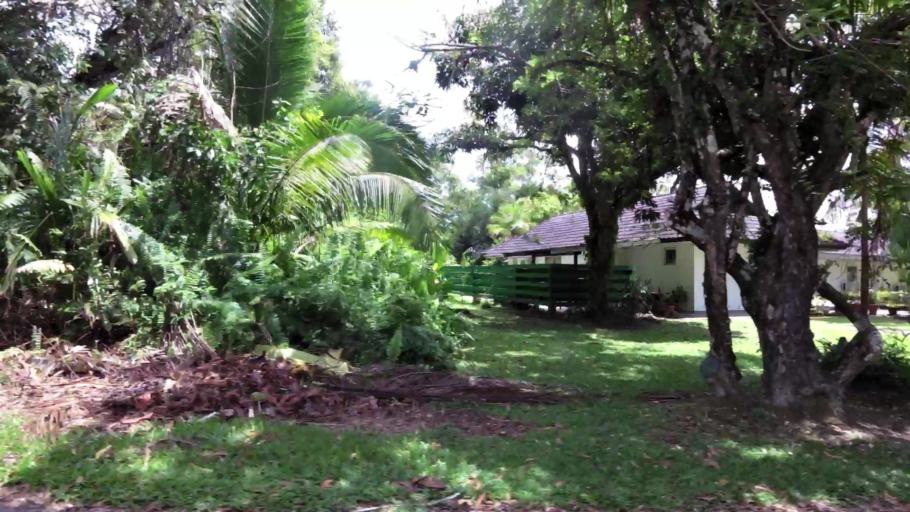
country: BN
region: Belait
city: Kuala Belait
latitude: 4.5981
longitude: 114.2718
